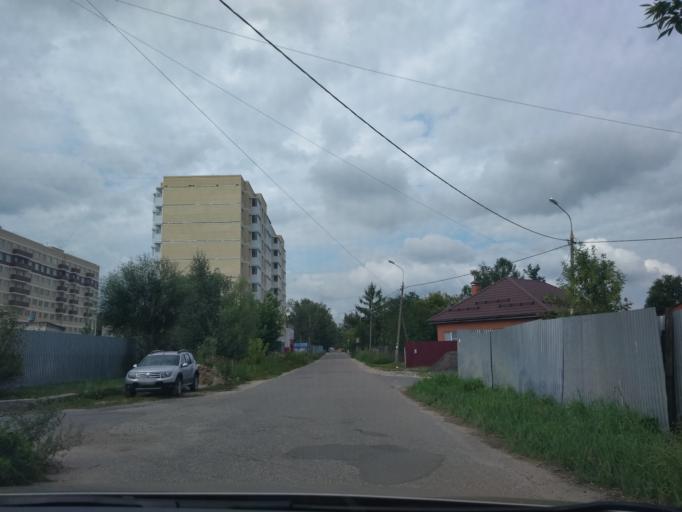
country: RU
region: Moskovskaya
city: Kabanovo
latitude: 55.7857
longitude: 38.9264
